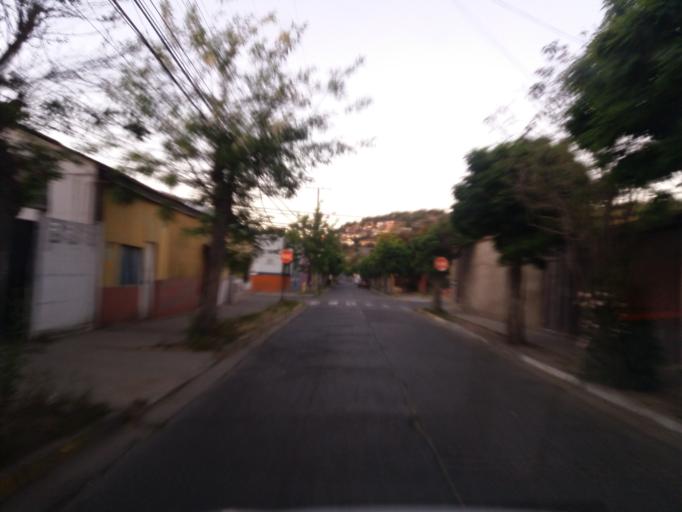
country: CL
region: Valparaiso
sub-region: Provincia de Quillota
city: Quillota
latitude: -32.8794
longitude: -71.2521
